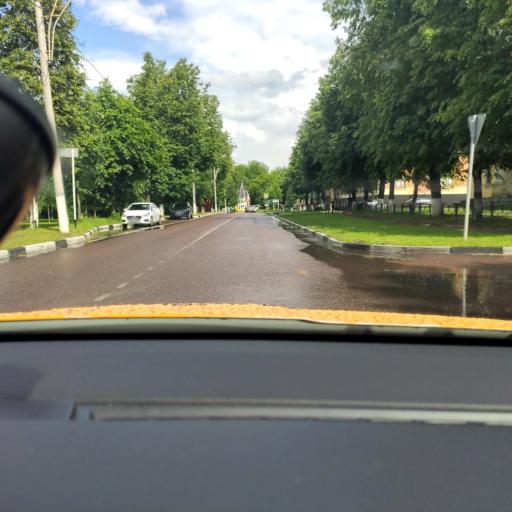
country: RU
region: Moskovskaya
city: Stupino
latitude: 54.8898
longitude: 38.0767
